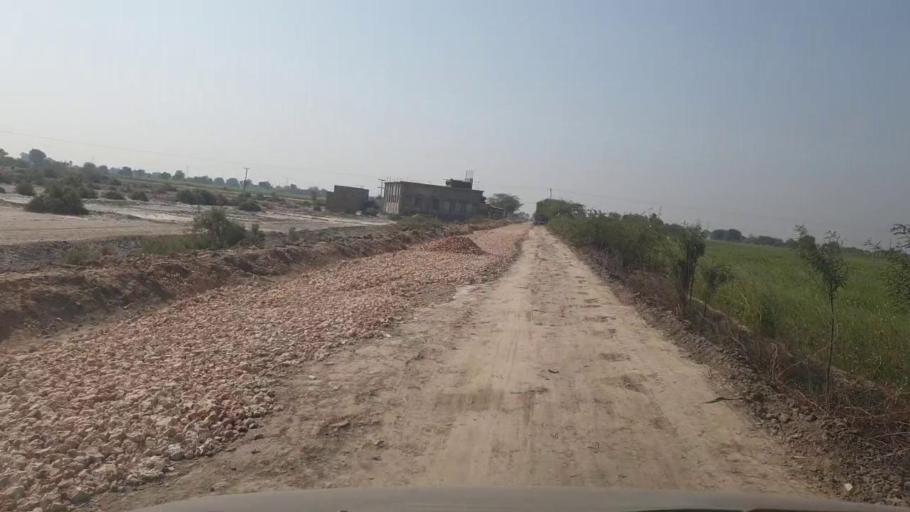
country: PK
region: Sindh
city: Mirwah Gorchani
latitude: 25.2566
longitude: 69.1136
